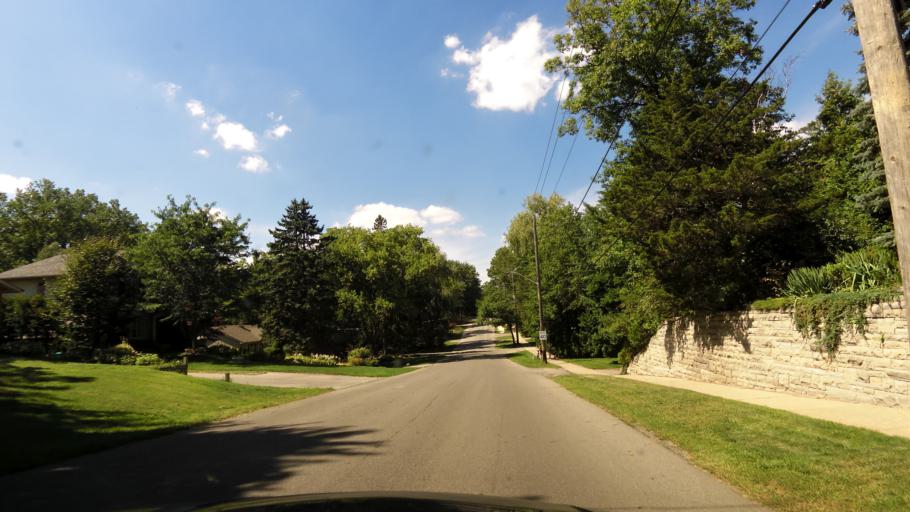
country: CA
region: Ontario
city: Mississauga
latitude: 43.5330
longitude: -79.6153
